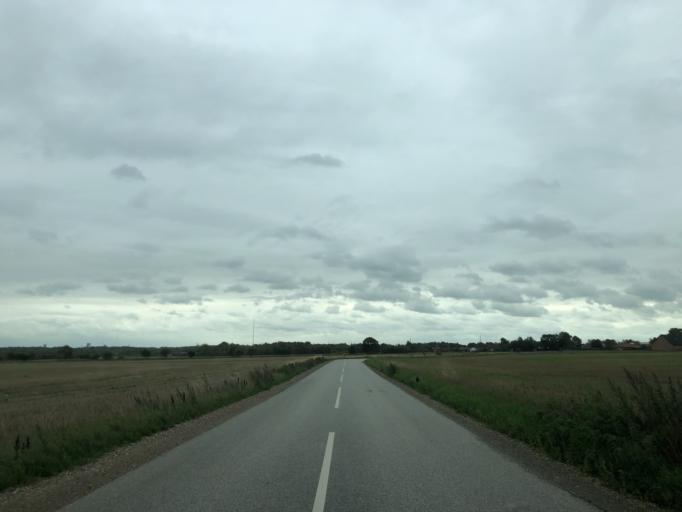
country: DK
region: Central Jutland
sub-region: Herning Kommune
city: Snejbjerg
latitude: 56.1421
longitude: 8.9043
